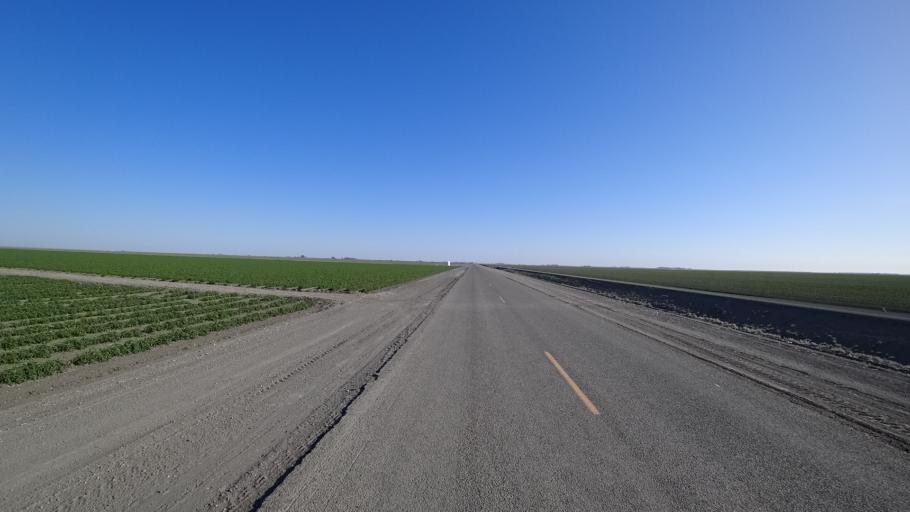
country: US
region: California
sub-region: Kings County
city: Stratford
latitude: 36.1207
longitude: -119.7981
